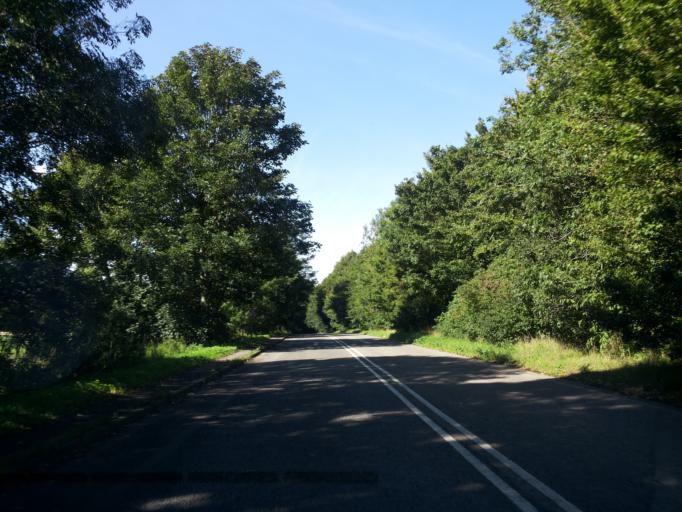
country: GB
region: England
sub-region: Kent
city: Canterbury
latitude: 51.2542
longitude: 1.1153
